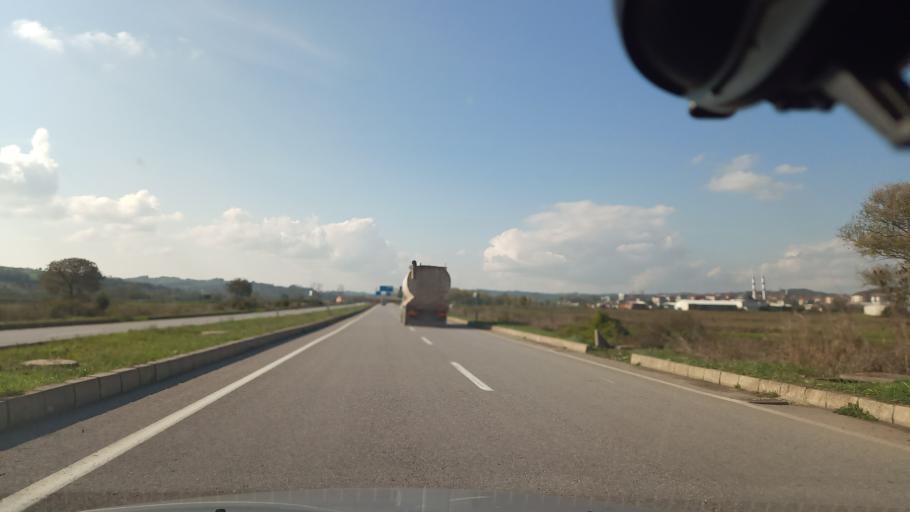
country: TR
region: Sakarya
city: Kaynarca
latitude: 41.0262
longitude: 30.3164
